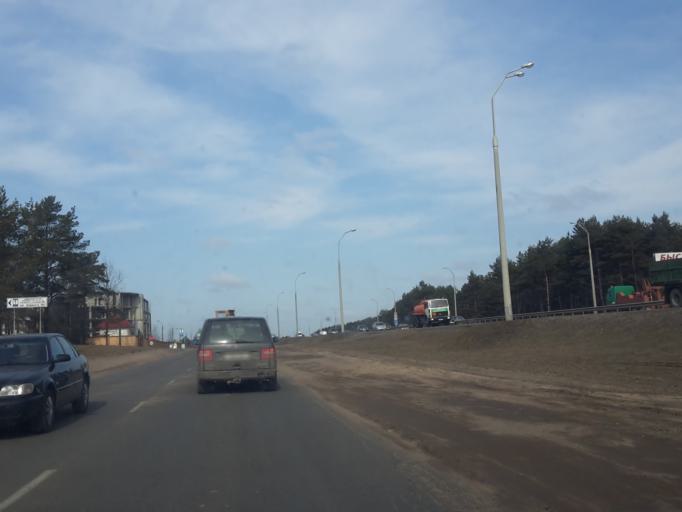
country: BY
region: Minsk
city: Vyaliki Trastsyanets
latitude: 53.9048
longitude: 27.6875
